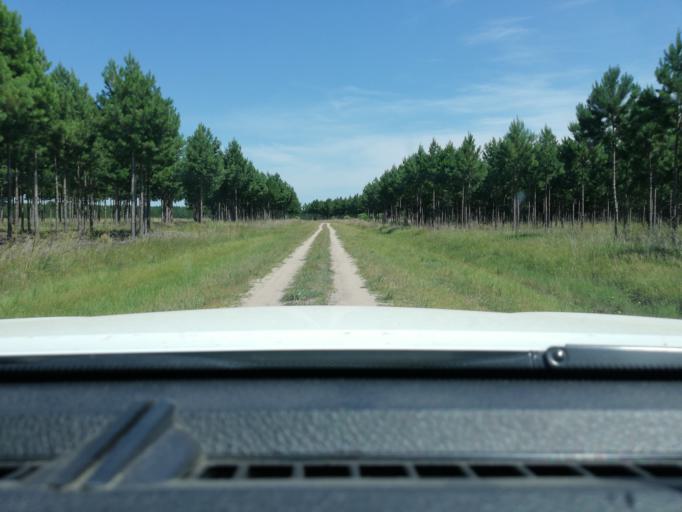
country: AR
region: Corrientes
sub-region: Departamento de San Miguel
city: San Miguel
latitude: -28.0323
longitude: -57.4685
